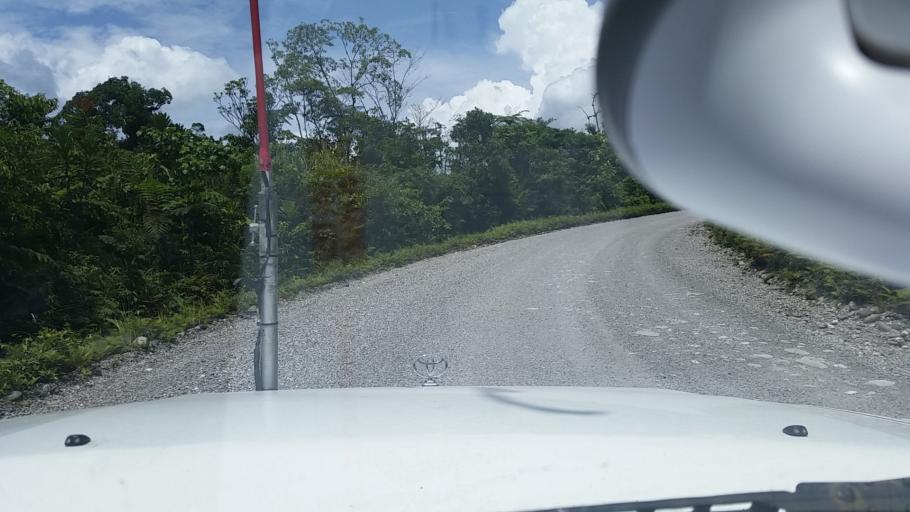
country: PG
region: Western Province
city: Kiunga
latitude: -5.3898
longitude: 141.2913
